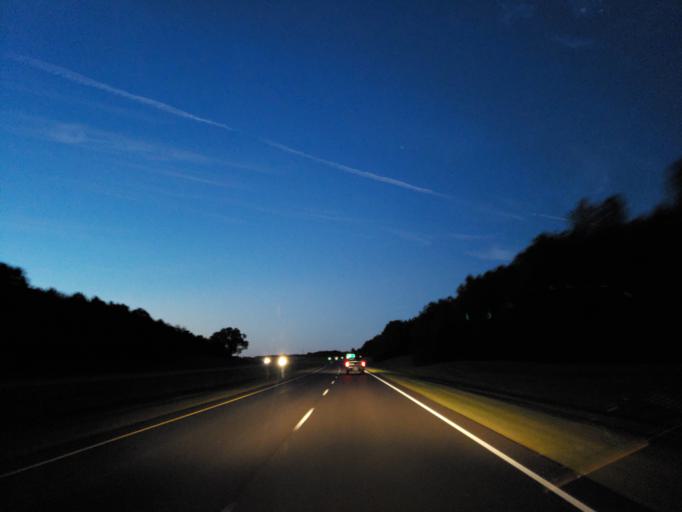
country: US
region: Mississippi
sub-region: Clarke County
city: Quitman
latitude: 32.0514
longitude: -88.6765
